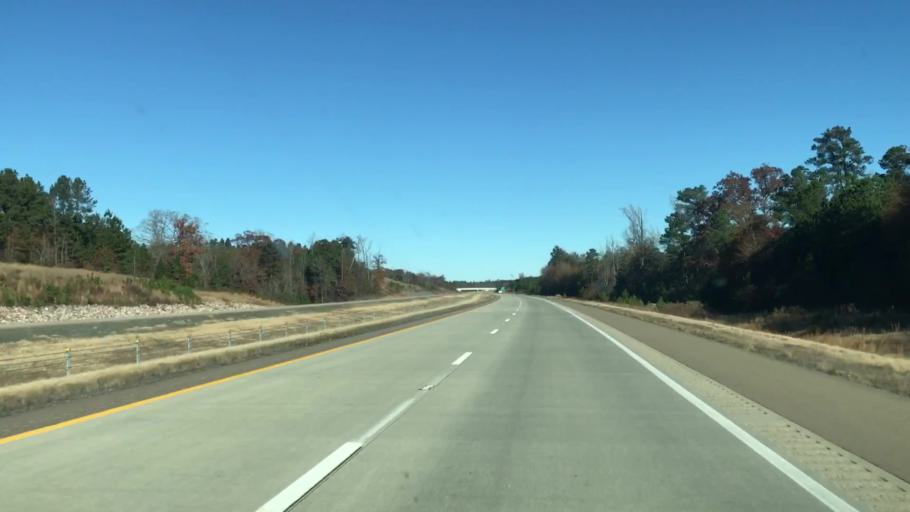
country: US
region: Louisiana
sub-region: Caddo Parish
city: Vivian
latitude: 33.0526
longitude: -93.9009
